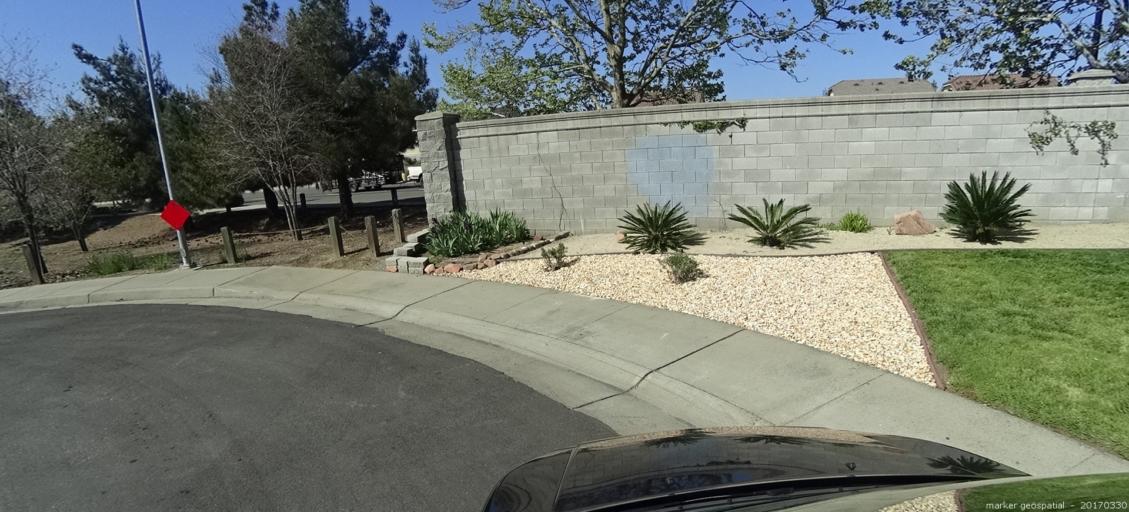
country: US
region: California
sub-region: Sacramento County
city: Laguna
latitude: 38.4430
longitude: -121.4174
